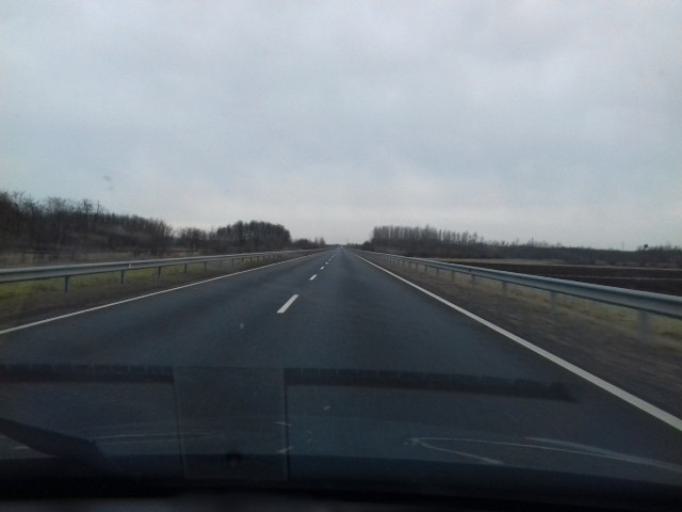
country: HU
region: Szabolcs-Szatmar-Bereg
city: Nyirpazony
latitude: 47.9775
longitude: 21.8183
